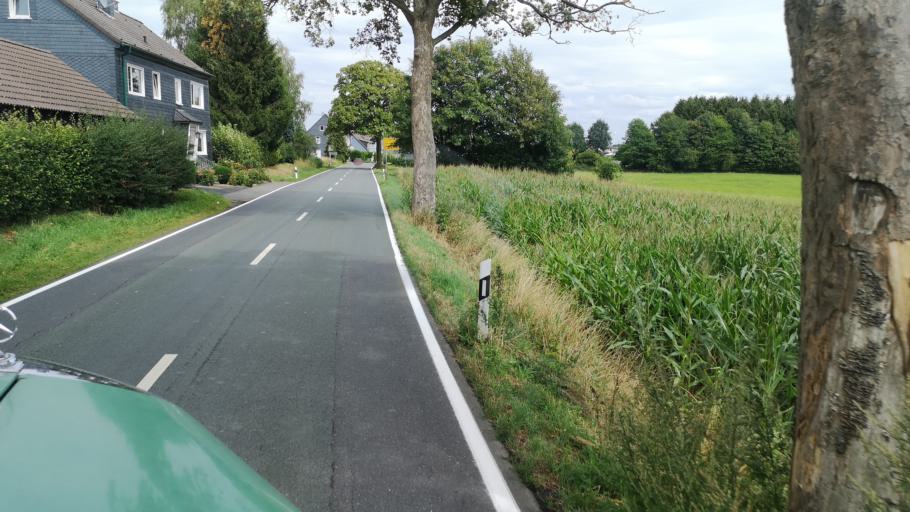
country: DE
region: North Rhine-Westphalia
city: Wermelskirchen
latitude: 51.1328
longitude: 7.2687
